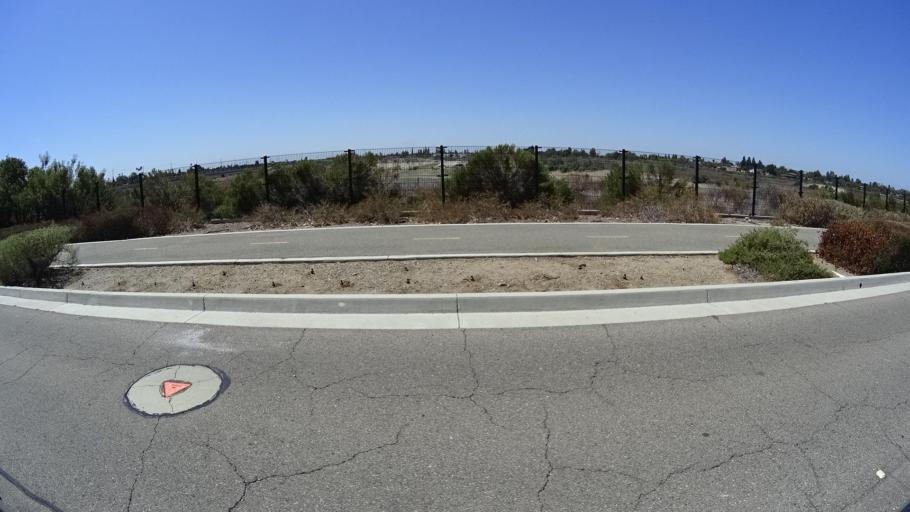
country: US
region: California
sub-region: Orange County
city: Villa Park
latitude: 33.8019
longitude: -117.8057
